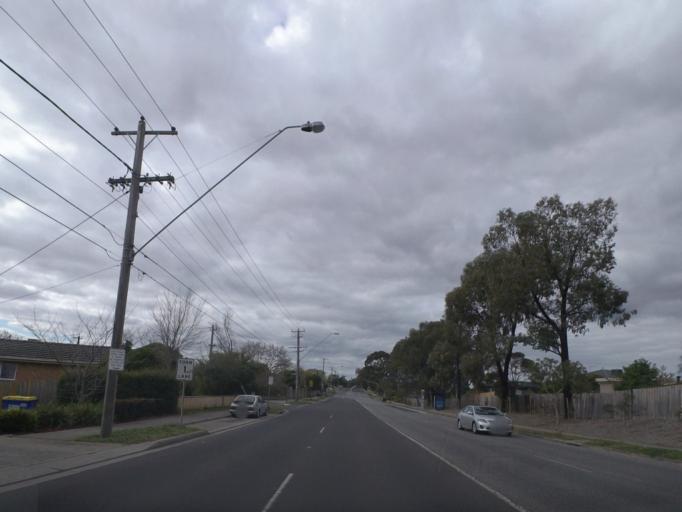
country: AU
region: Victoria
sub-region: Manningham
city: Templestowe Lower
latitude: -37.7692
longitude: 145.1175
